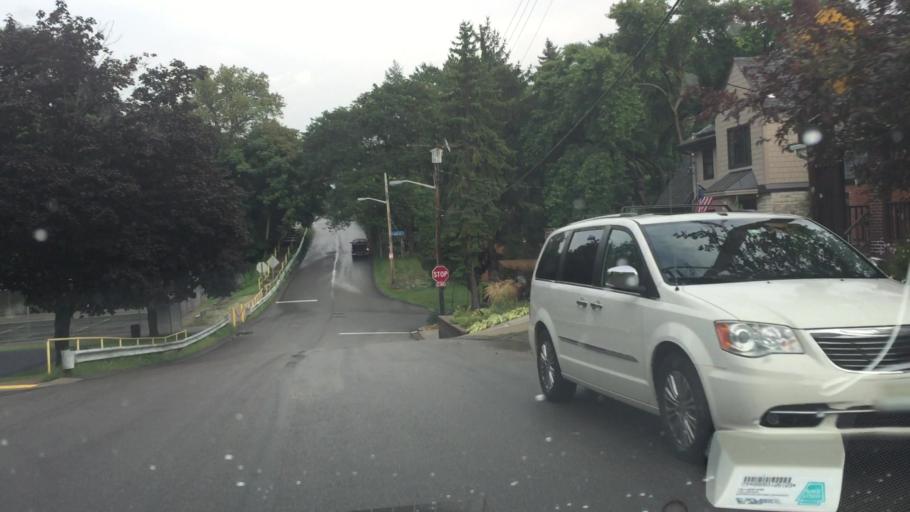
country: US
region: Pennsylvania
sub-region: Allegheny County
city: Sharpsburg
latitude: 40.4768
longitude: -79.9287
